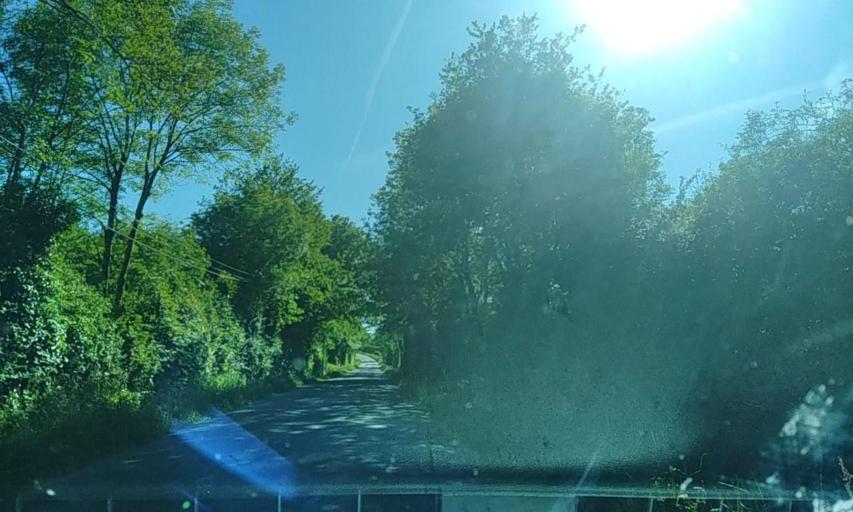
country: FR
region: Poitou-Charentes
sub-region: Departement des Deux-Sevres
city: Boisme
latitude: 46.7965
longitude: -0.4237
